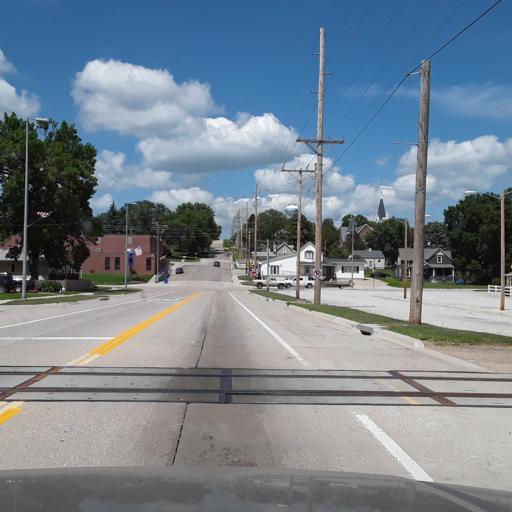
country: US
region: Nebraska
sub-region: Nance County
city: Genoa
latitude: 41.4474
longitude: -97.7346
